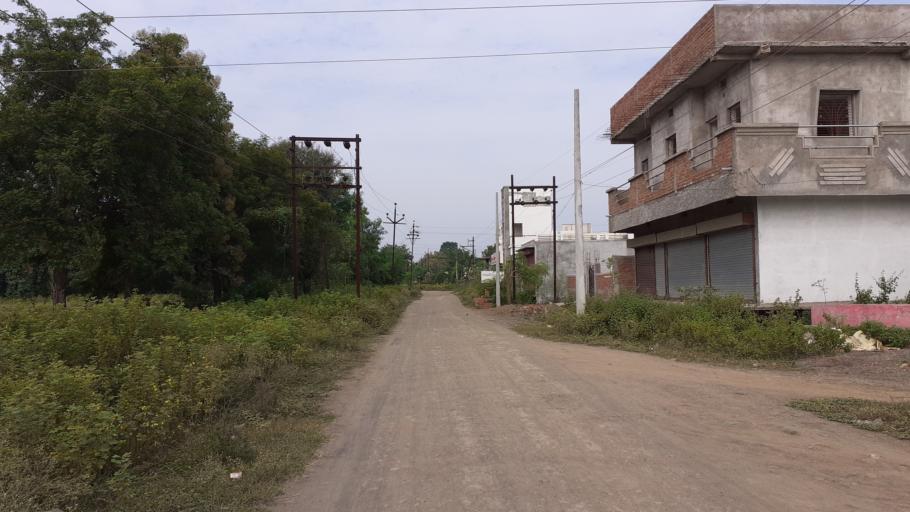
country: IN
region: Maharashtra
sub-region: Chandrapur
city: Warora
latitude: 20.2347
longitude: 79.0173
